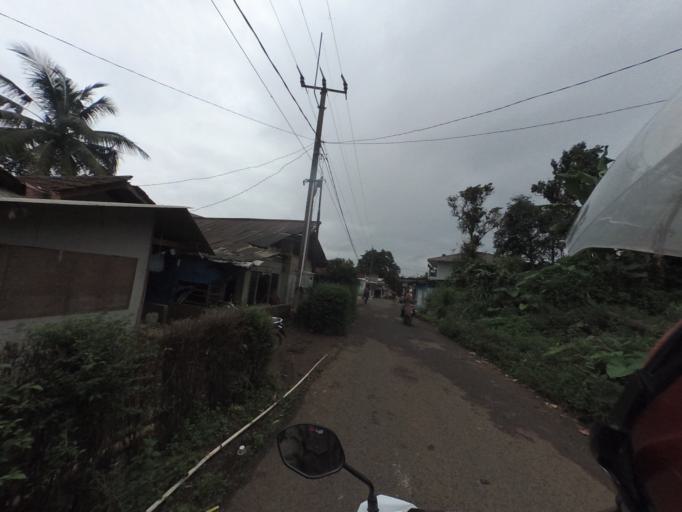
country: ID
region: West Java
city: Bogor
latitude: -6.6358
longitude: 106.7294
